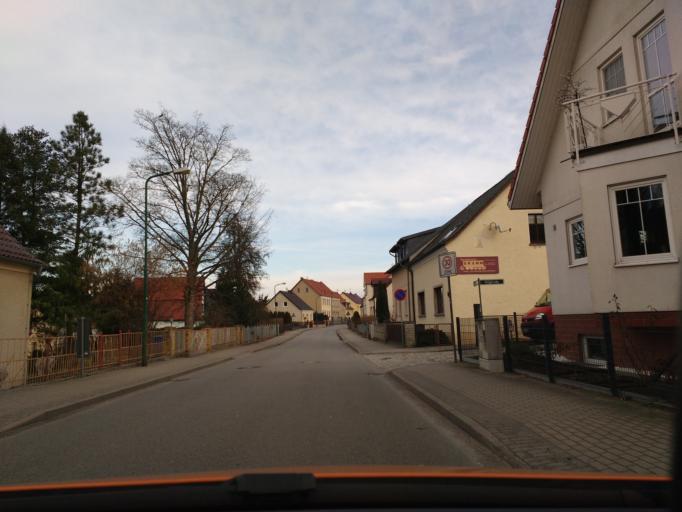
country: DE
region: Brandenburg
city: Michendorf
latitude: 52.3421
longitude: 12.9825
